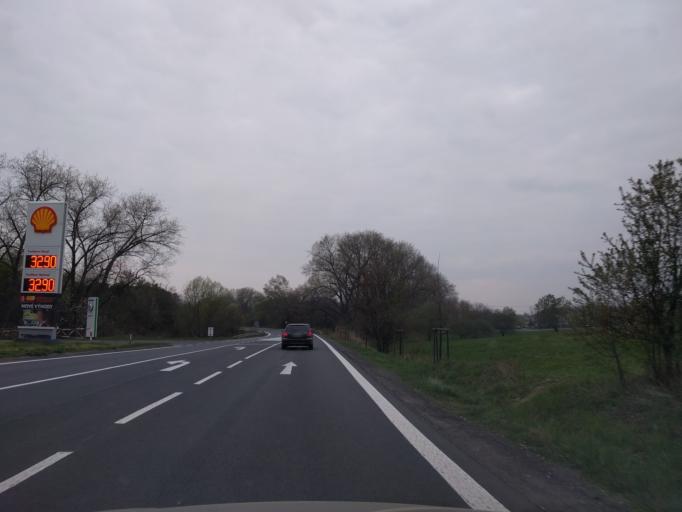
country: CZ
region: Central Bohemia
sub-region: Okres Praha-Vychod
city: Ricany
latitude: 49.9985
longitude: 14.6556
